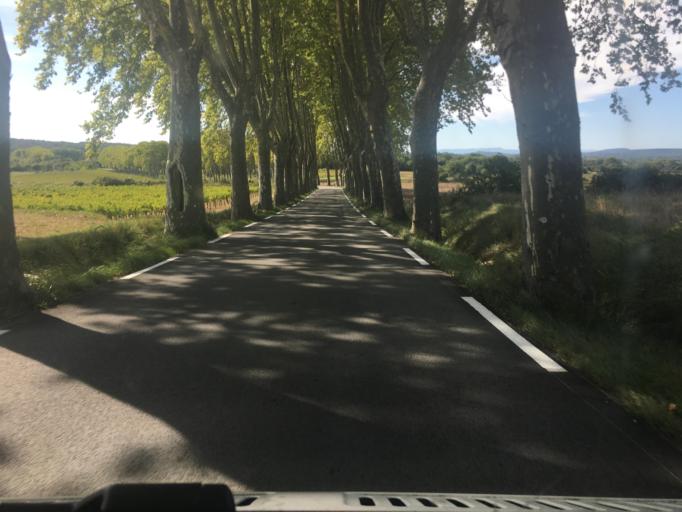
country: FR
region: Languedoc-Roussillon
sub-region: Departement du Gard
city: Saint-Quentin-la-Poterie
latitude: 44.0309
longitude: 4.4788
